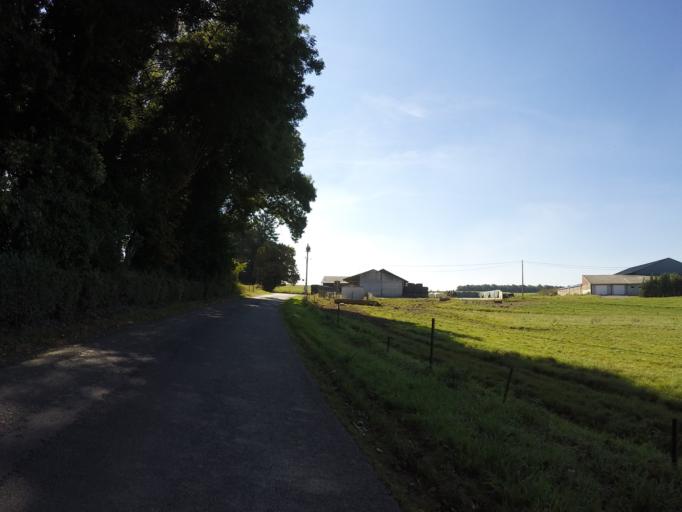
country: BE
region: Wallonia
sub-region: Province de Namur
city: Assesse
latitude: 50.3020
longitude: 5.0286
